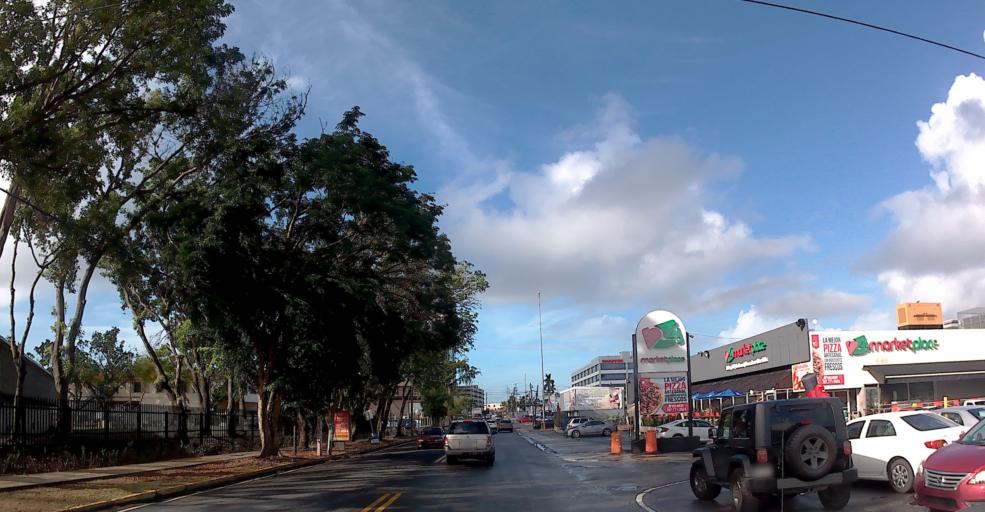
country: PR
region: Catano
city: Catano
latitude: 18.4246
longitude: -66.0647
